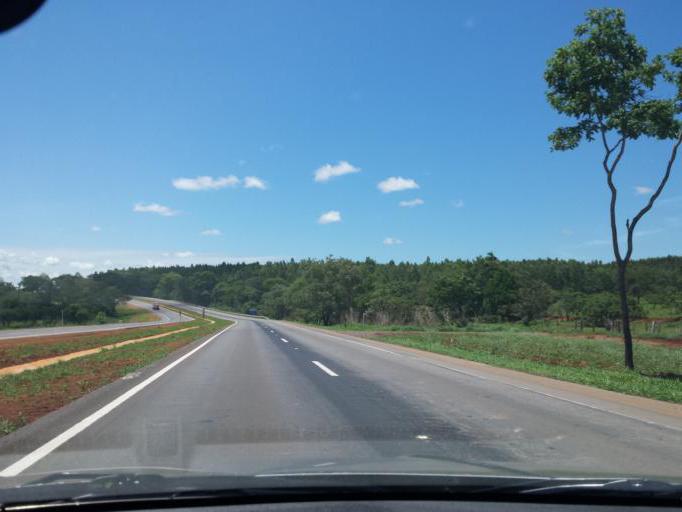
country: BR
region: Goias
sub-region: Luziania
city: Luziania
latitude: -16.4877
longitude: -47.8136
